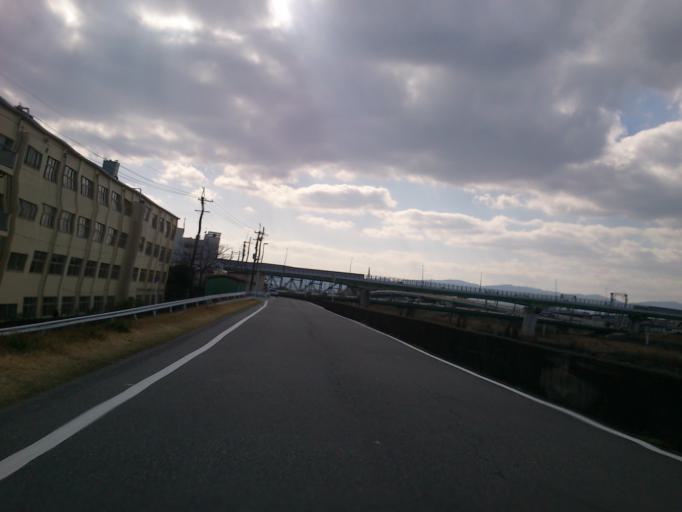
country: JP
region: Kyoto
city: Uji
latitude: 34.9273
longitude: 135.7721
